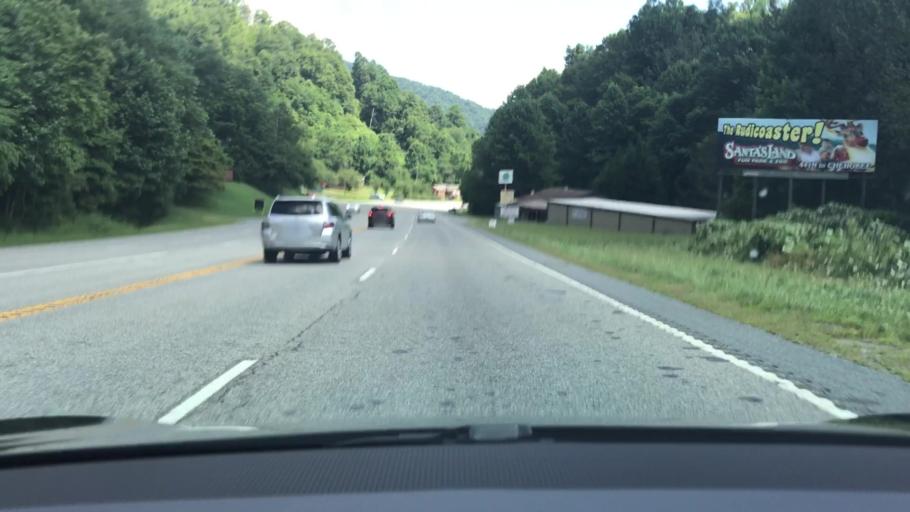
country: US
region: North Carolina
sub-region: Jackson County
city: Sylva
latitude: 35.2766
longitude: -83.2890
